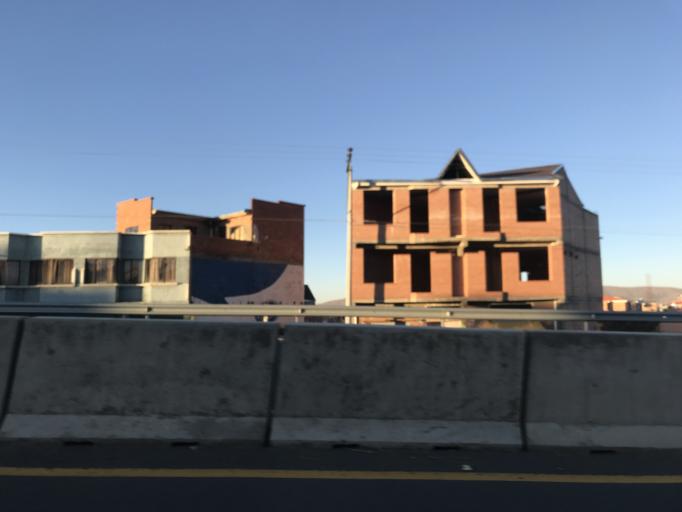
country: BO
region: La Paz
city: Batallas
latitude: -16.2980
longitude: -68.5292
